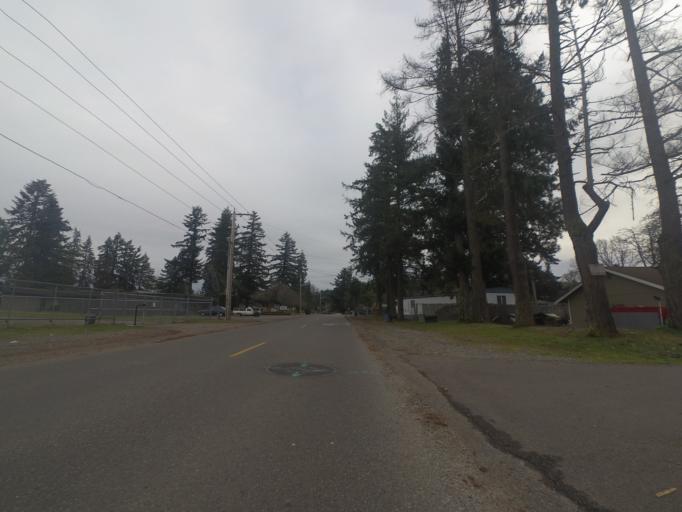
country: US
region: Washington
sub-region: Pierce County
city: McChord Air Force Base
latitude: 47.1249
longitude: -122.5298
